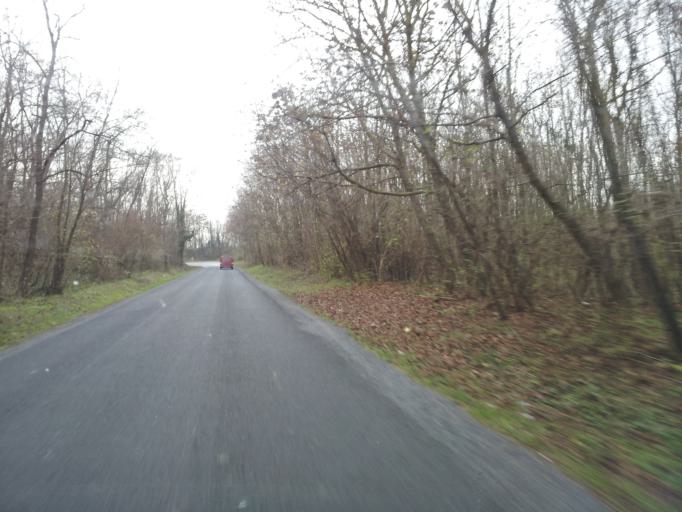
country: HU
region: Zala
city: Cserszegtomaj
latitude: 46.8707
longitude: 17.2148
